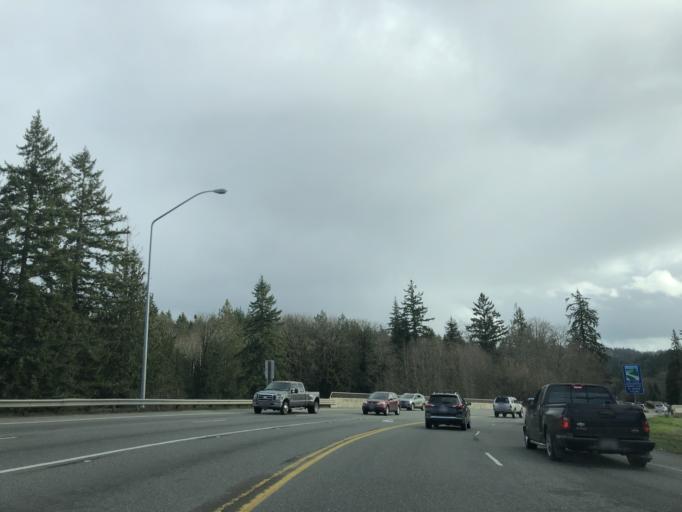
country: US
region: Washington
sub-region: Kitsap County
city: Poulsbo
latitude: 47.7571
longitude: -122.6521
